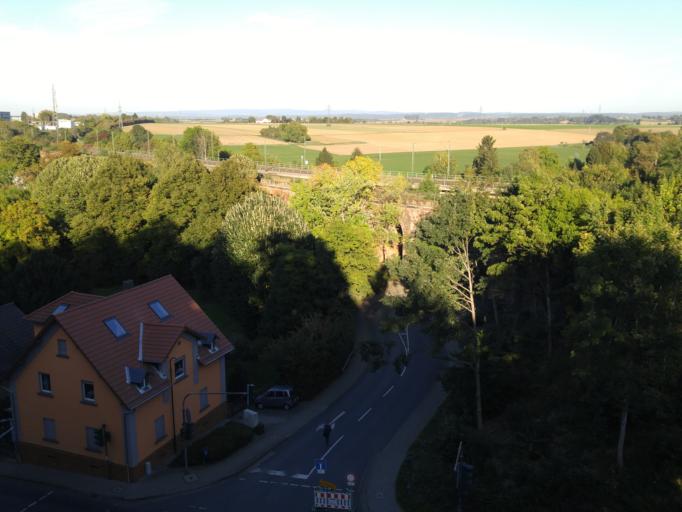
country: DE
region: Hesse
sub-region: Regierungsbezirk Darmstadt
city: Friedberg
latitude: 50.3408
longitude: 8.7558
